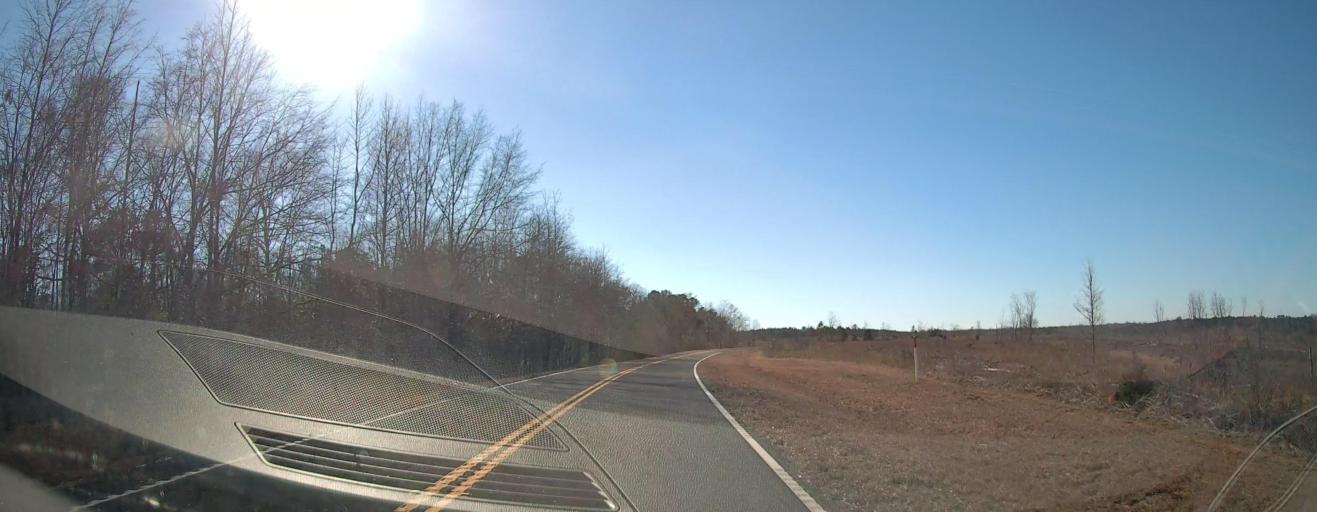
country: US
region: Georgia
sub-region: Talbot County
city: Talbotton
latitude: 32.6478
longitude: -84.4005
